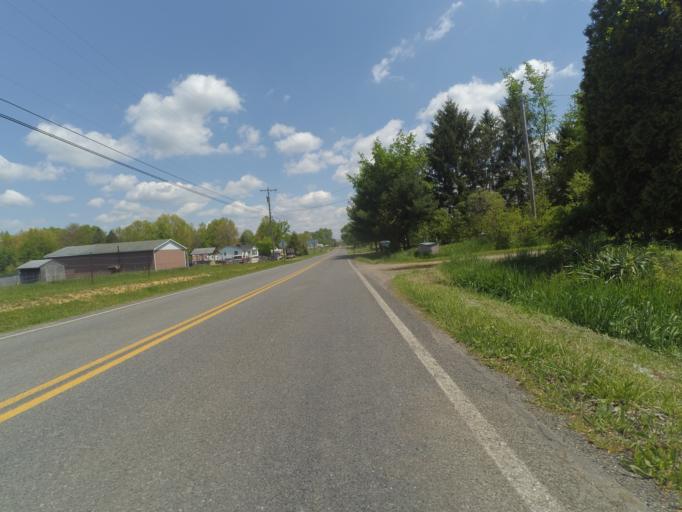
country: US
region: Ohio
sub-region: Portage County
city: Ravenna
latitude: 41.1371
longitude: -81.2187
